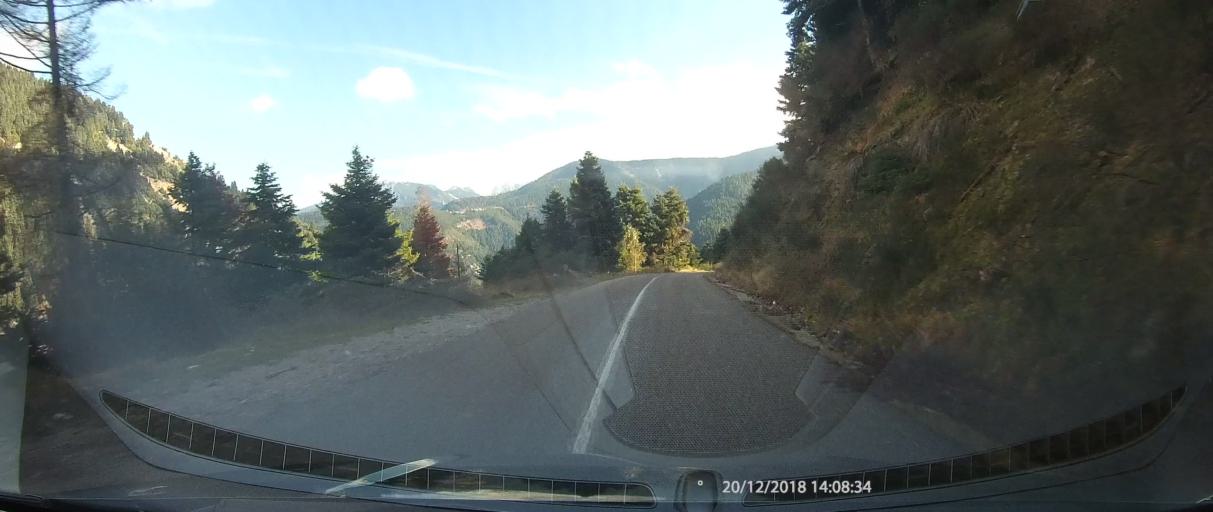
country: GR
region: West Greece
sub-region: Nomos Aitolias kai Akarnanias
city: Thermo
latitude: 38.7549
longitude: 21.6466
